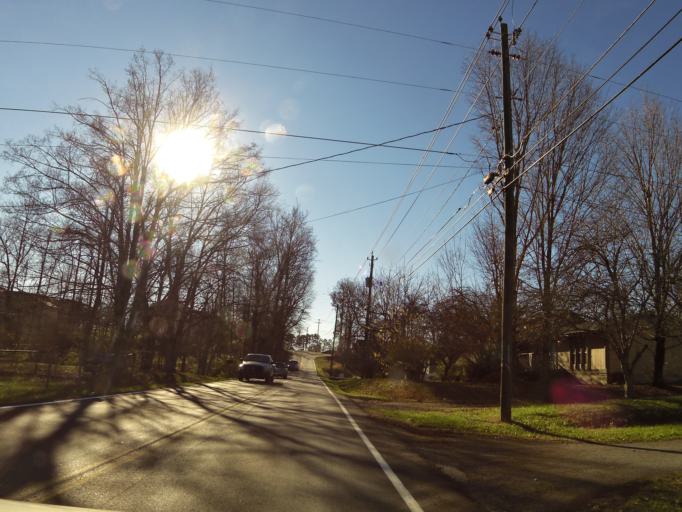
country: US
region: Tennessee
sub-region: Knox County
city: Knoxville
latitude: 36.0325
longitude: -83.9830
